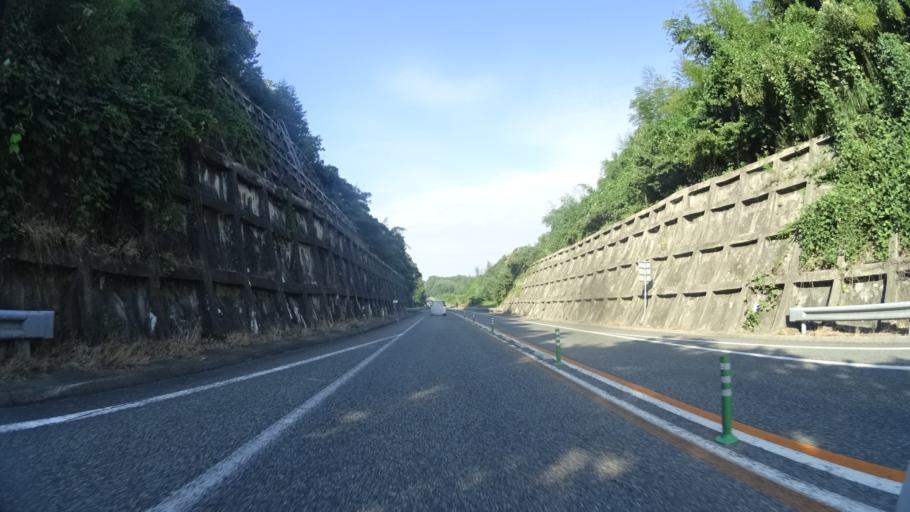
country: JP
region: Shimane
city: Matsue-shi
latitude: 35.4102
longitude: 132.9448
